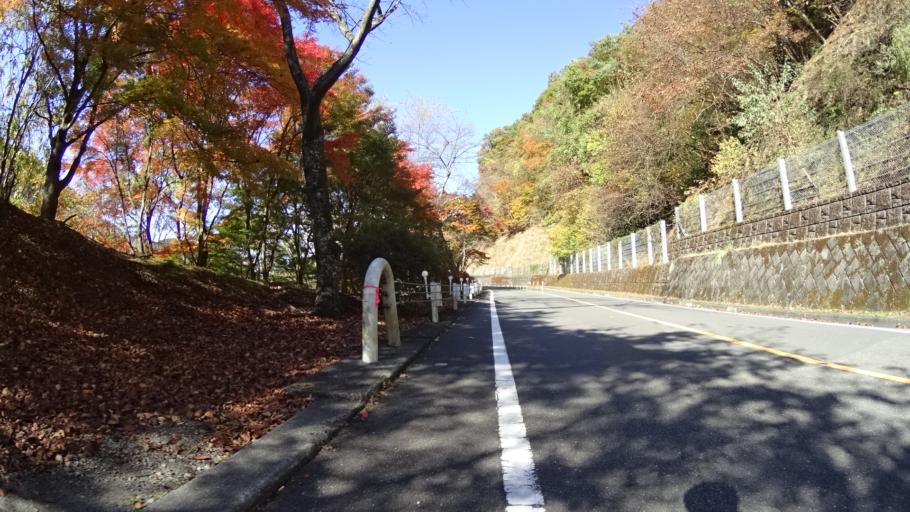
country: JP
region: Yamanashi
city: Uenohara
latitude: 35.7564
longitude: 139.0275
